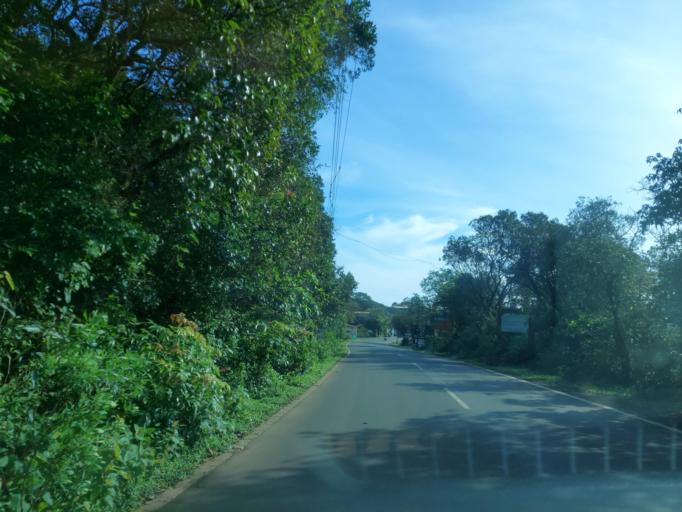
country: IN
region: Maharashtra
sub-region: Sindhudurg
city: Savantvadi
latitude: 15.9613
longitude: 73.9956
